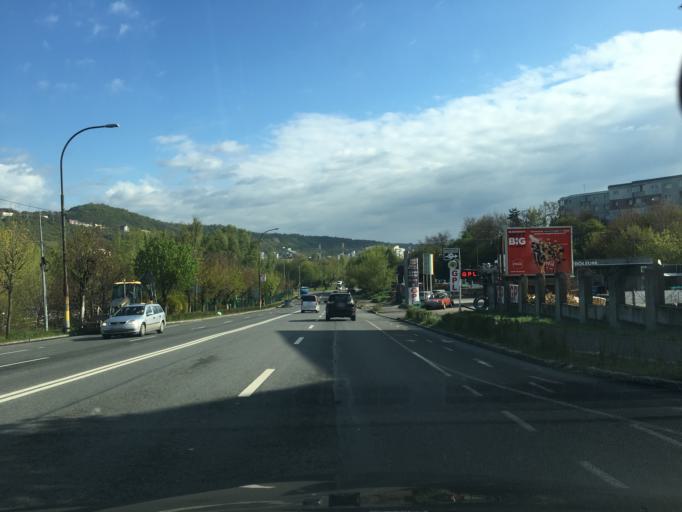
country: RO
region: Cluj
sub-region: Comuna Baciu
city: Baciu
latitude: 46.7589
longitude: 23.5432
